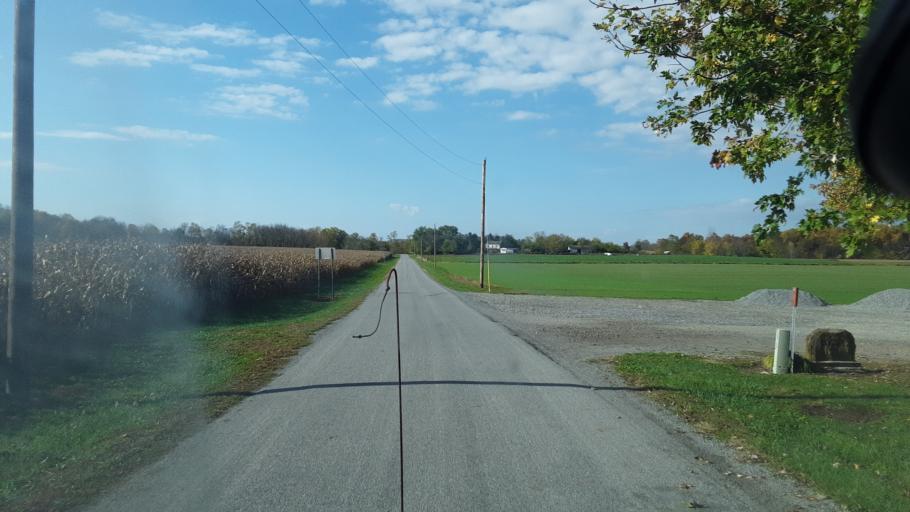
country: US
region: Ohio
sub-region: Highland County
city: Leesburg
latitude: 39.3150
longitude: -83.4988
